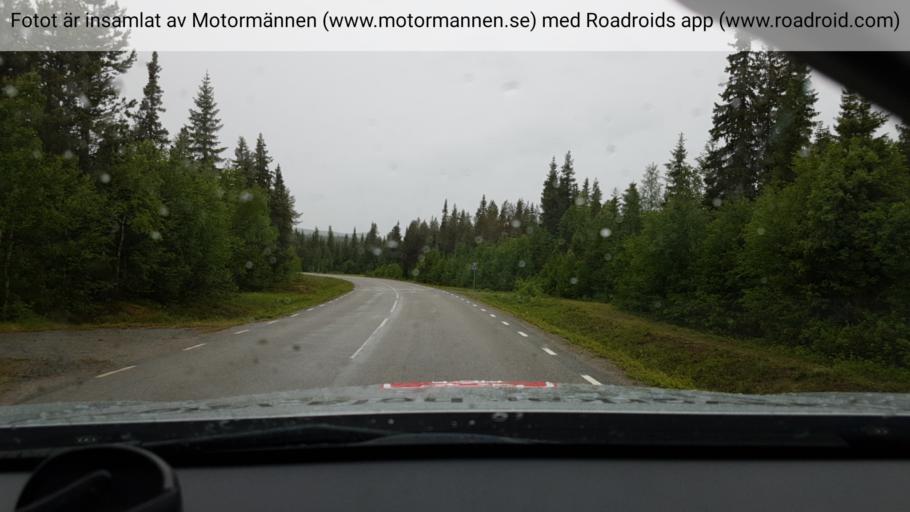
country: SE
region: Vaesterbotten
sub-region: Storumans Kommun
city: Fristad
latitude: 65.8540
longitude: 16.5006
